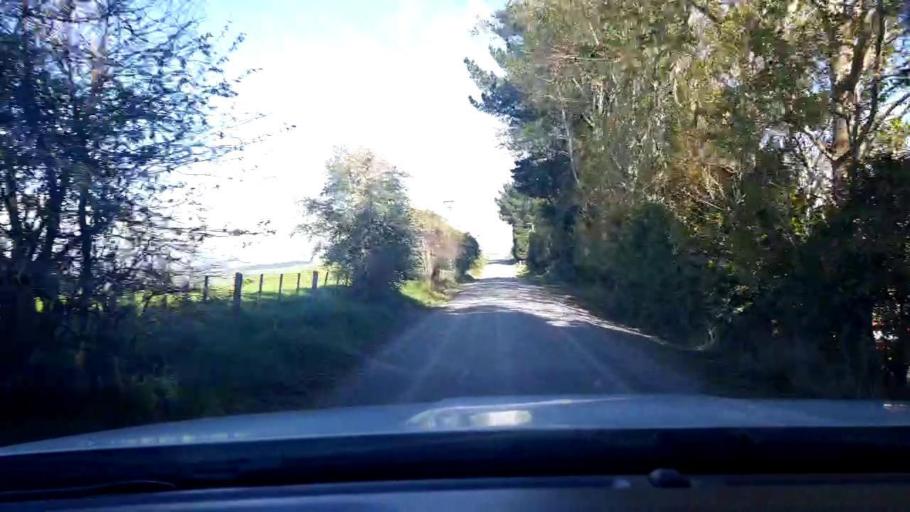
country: NZ
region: Otago
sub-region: Clutha District
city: Balclutha
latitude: -46.2237
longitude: 169.7572
